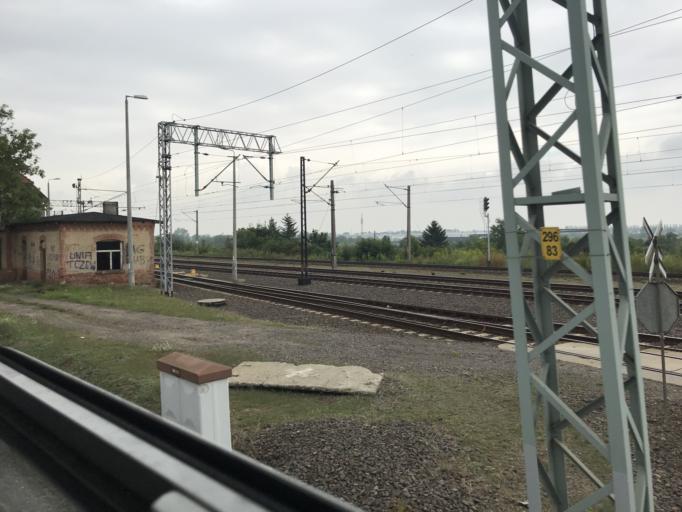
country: PL
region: Pomeranian Voivodeship
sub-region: Powiat tczewski
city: Tczew
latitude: 54.1012
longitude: 18.7860
